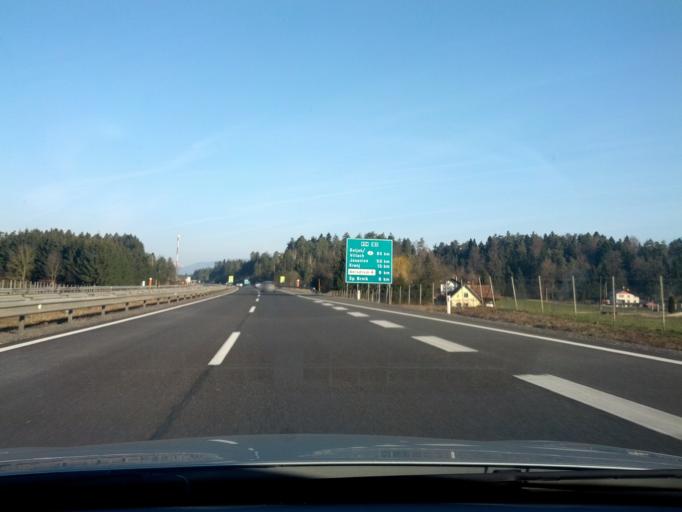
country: SI
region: Vodice
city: Vodice
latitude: 46.1853
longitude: 14.4826
